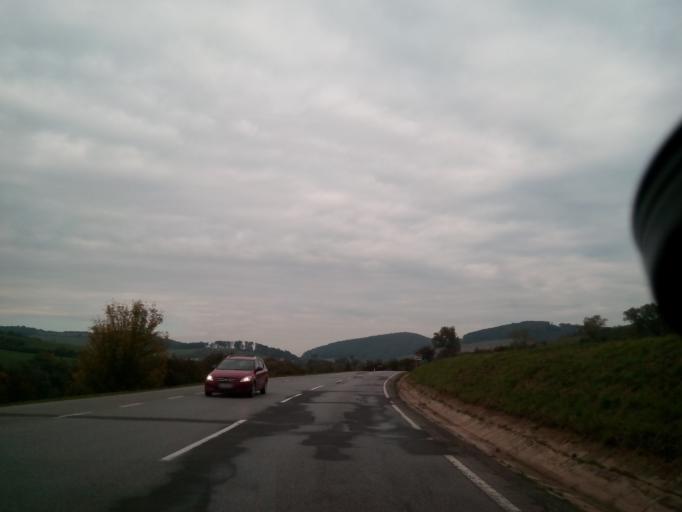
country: SK
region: Presovsky
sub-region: Okres Presov
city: Presov
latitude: 49.0943
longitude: 21.3118
